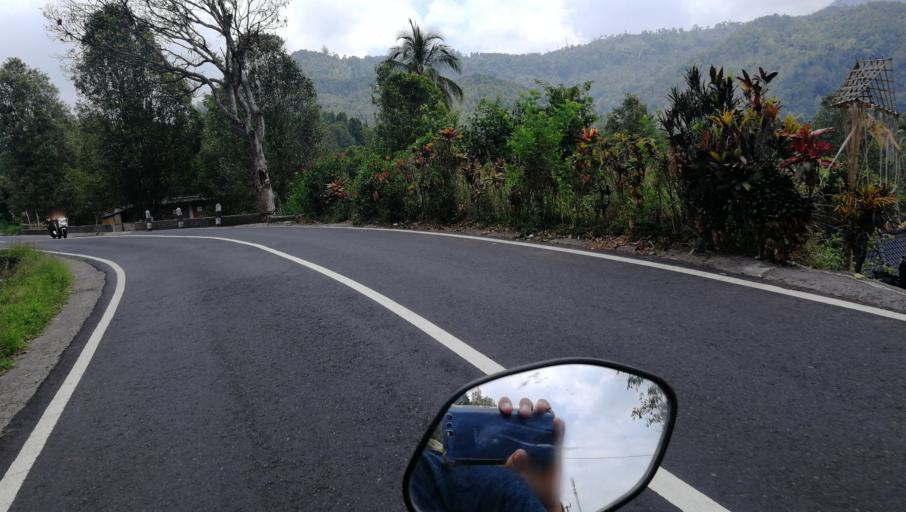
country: ID
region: Bali
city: Munduk
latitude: -8.2639
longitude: 115.0615
